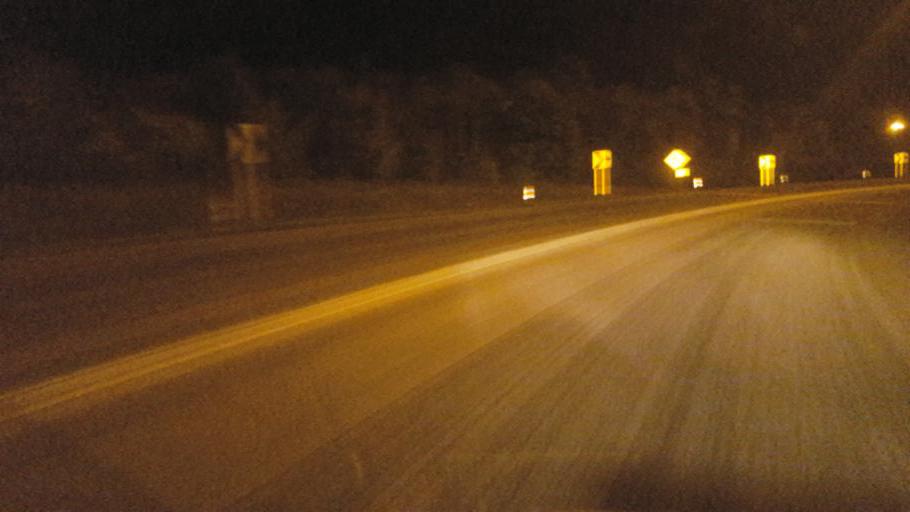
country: US
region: Ohio
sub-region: Richland County
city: Lincoln Heights
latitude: 40.7831
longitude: -82.4151
